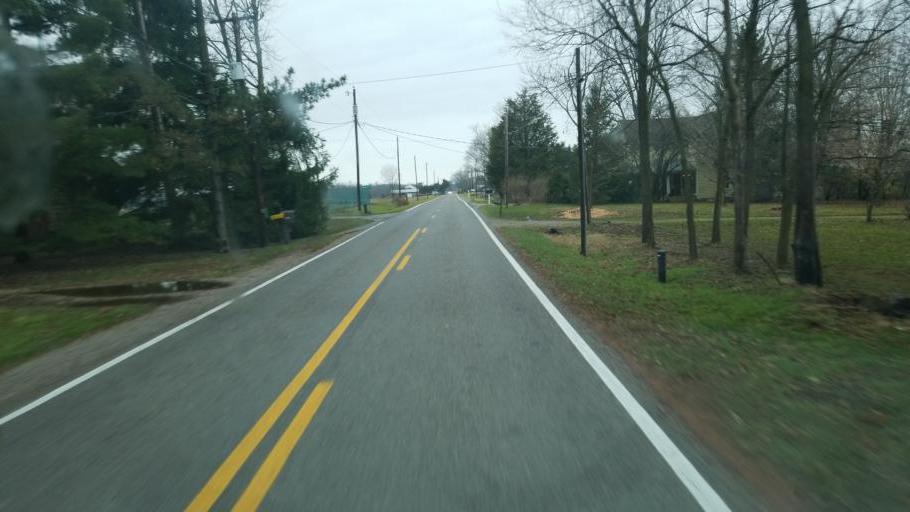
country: US
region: Ohio
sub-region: Delaware County
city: Ashley
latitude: 40.3573
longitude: -82.9912
